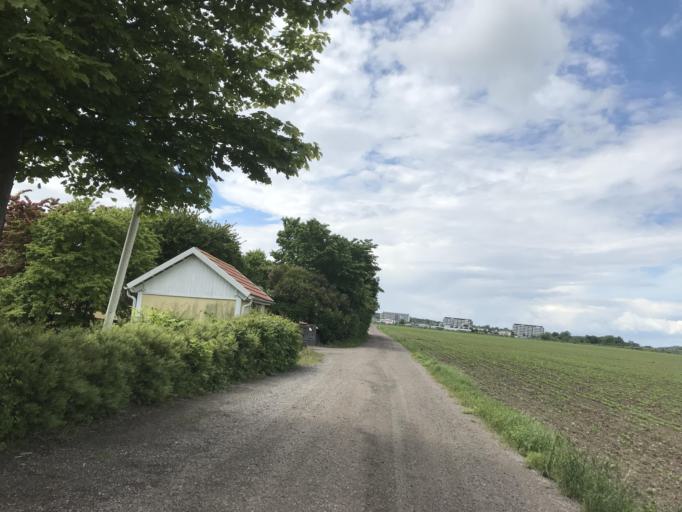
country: SE
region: Skane
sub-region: Landskrona
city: Landskrona
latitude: 55.8867
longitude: 12.8655
